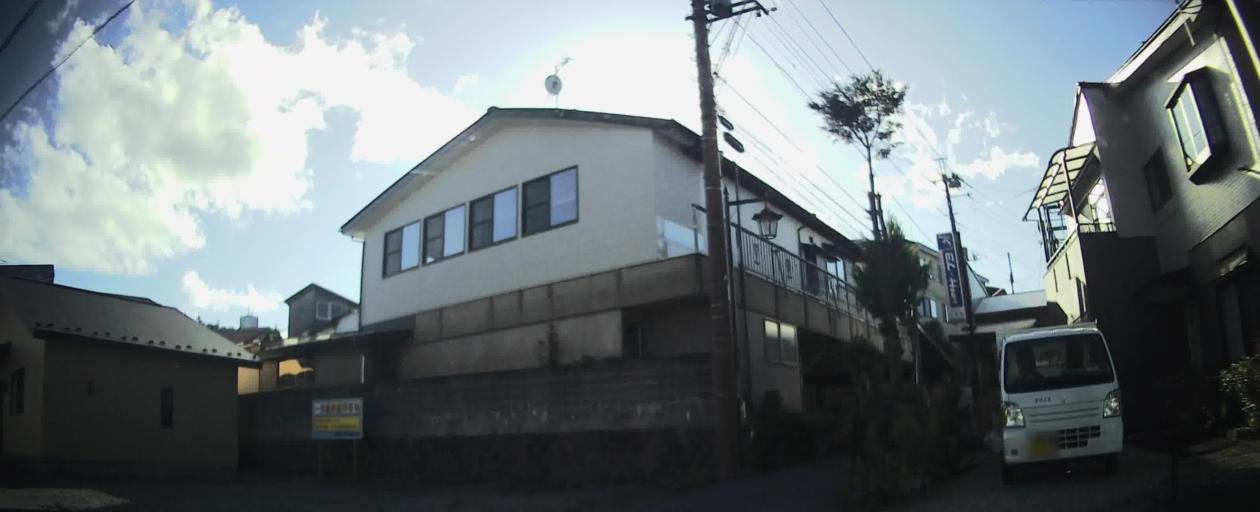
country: JP
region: Gunma
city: Nakanojomachi
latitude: 36.6216
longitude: 138.5993
